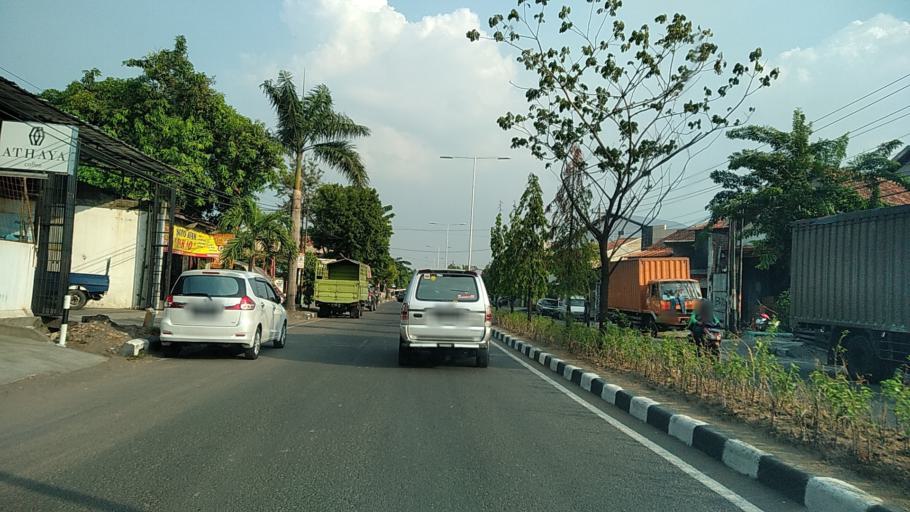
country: ID
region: Central Java
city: Semarang
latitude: -7.0010
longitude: 110.4666
